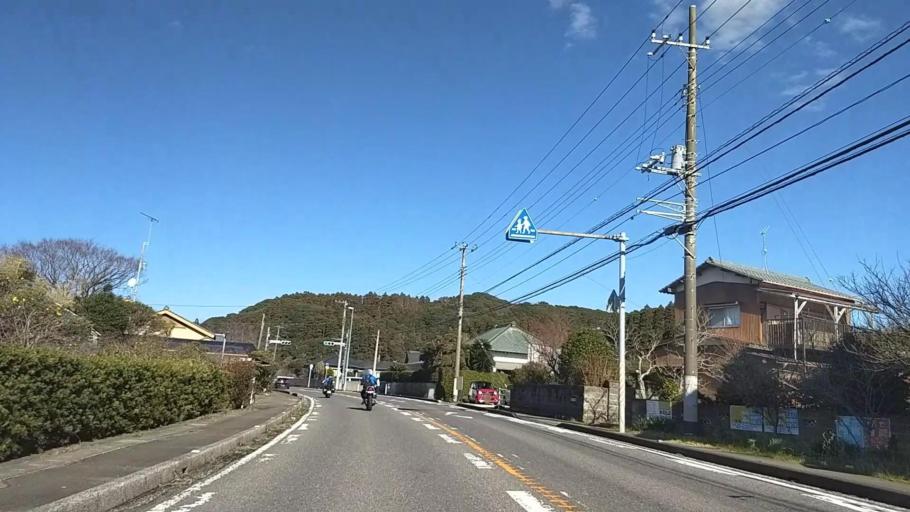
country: JP
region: Chiba
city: Ohara
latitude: 35.2237
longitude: 140.3853
